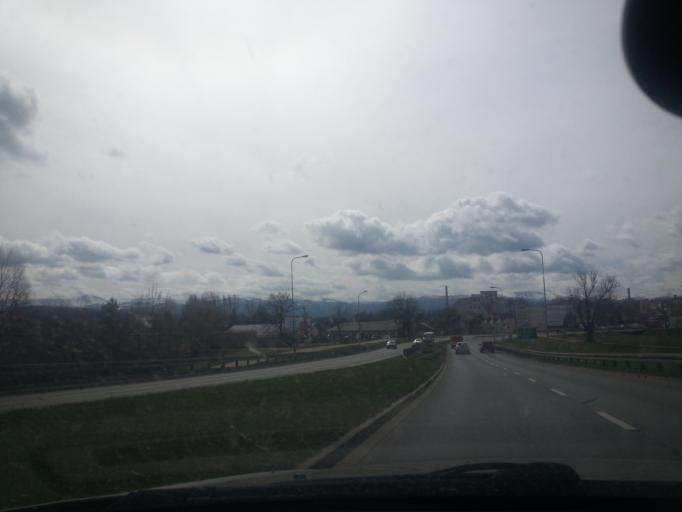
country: PL
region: Lower Silesian Voivodeship
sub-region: Jelenia Gora
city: Jelenia Gora
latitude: 50.9056
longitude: 15.7288
